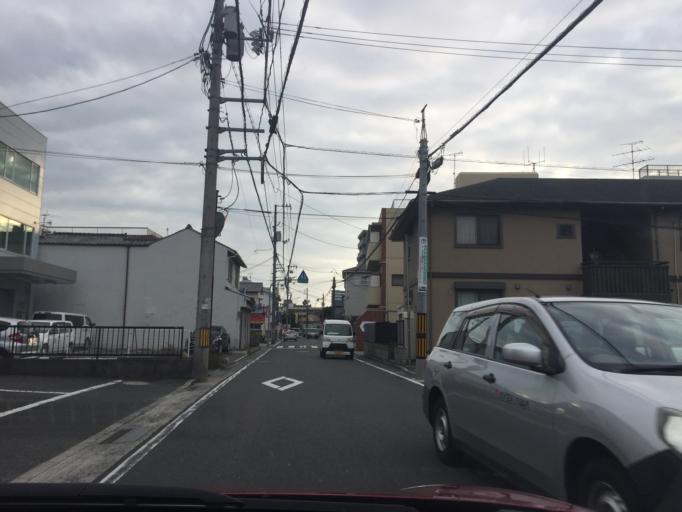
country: JP
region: Hiroshima
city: Hiroshima-shi
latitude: 34.4312
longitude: 132.4592
